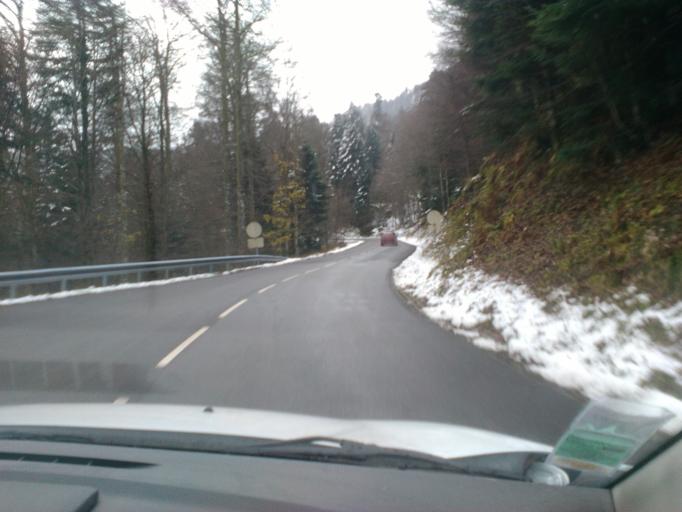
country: FR
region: Lorraine
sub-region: Departement des Vosges
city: Xonrupt-Longemer
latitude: 48.0499
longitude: 6.9873
